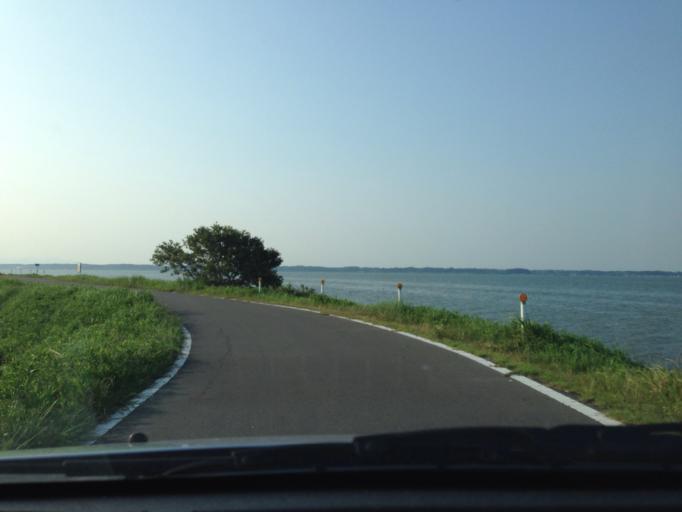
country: JP
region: Ibaraki
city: Inashiki
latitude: 36.0271
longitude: 140.3533
